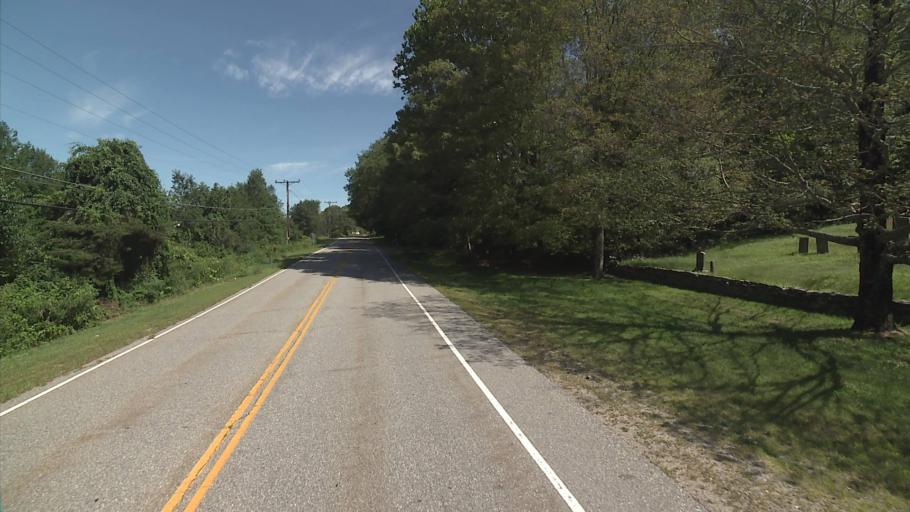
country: US
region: Connecticut
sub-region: New London County
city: Baltic
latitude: 41.6880
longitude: -72.0849
